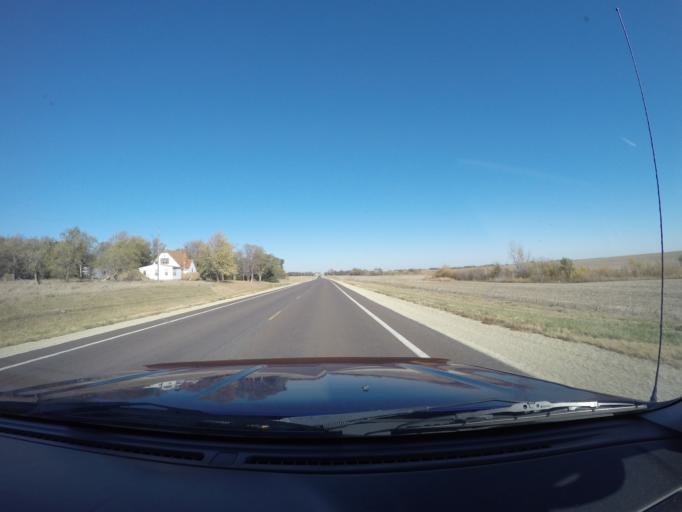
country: US
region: Kansas
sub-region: Marshall County
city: Blue Rapids
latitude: 39.6175
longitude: -96.7502
